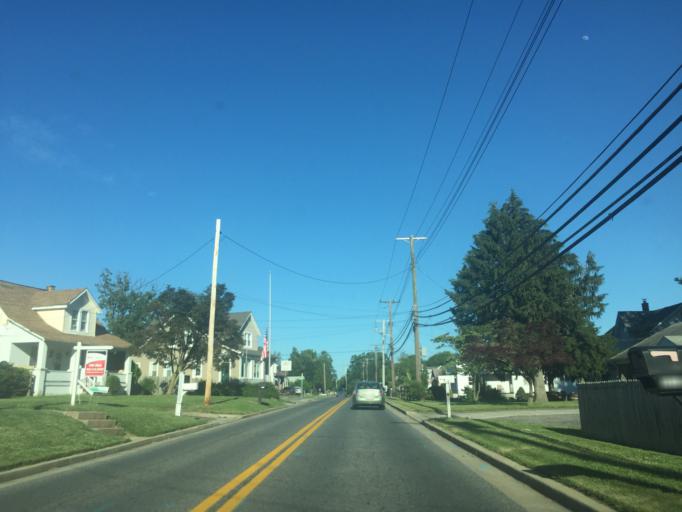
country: US
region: Maryland
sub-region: Baltimore County
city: Carney
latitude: 39.3804
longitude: -76.5253
